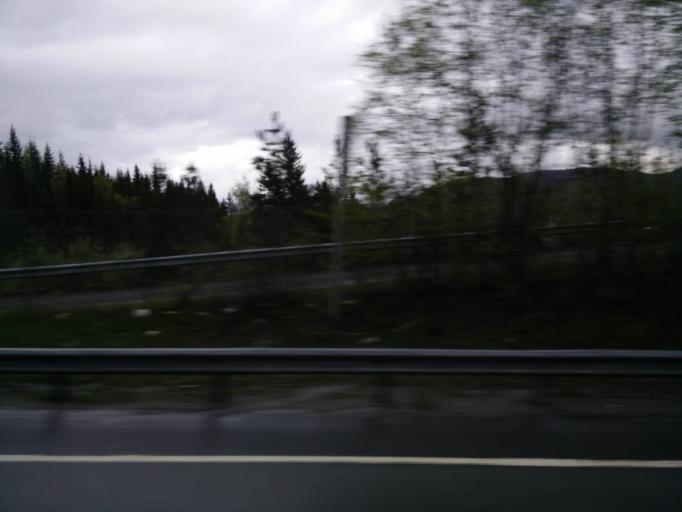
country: NO
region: Sor-Trondelag
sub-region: Malvik
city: Hommelvik
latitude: 63.4112
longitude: 10.7725
